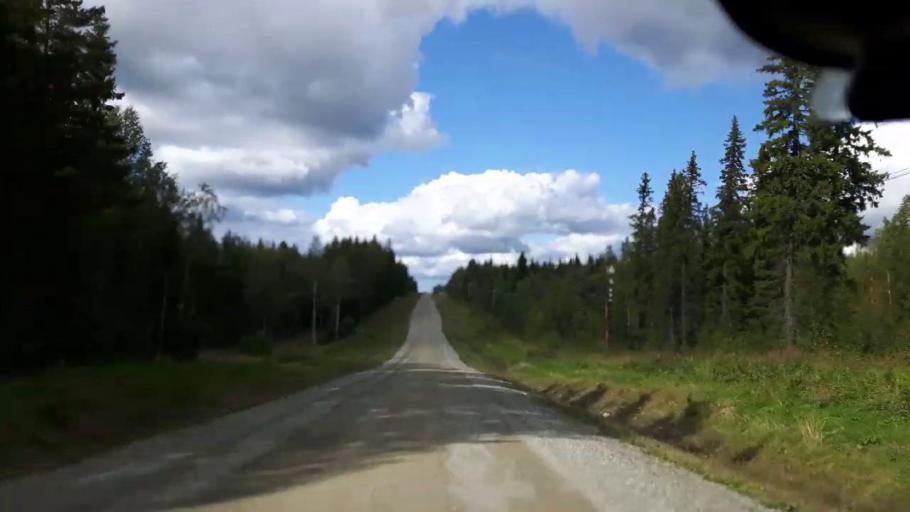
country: SE
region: Jaemtland
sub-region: Stroemsunds Kommun
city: Stroemsund
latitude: 63.3645
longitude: 15.5686
